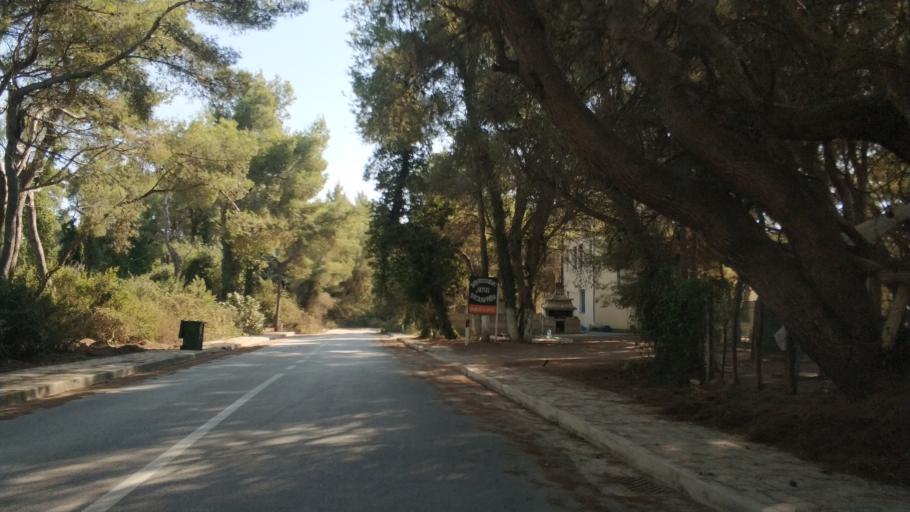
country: AL
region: Fier
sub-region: Rrethi i Lushnjes
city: Divjake
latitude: 40.9641
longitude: 19.4773
